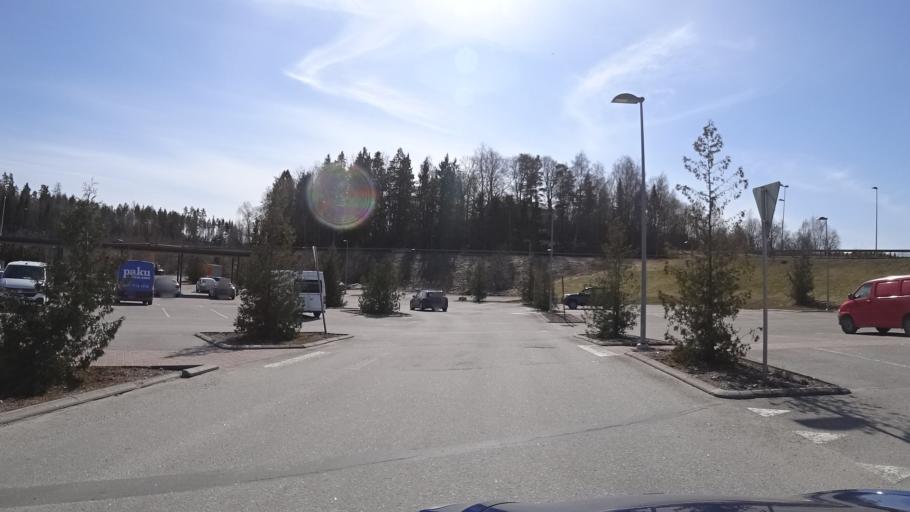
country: FI
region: Uusimaa
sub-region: Helsinki
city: Lohja
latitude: 60.2933
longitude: 24.0620
